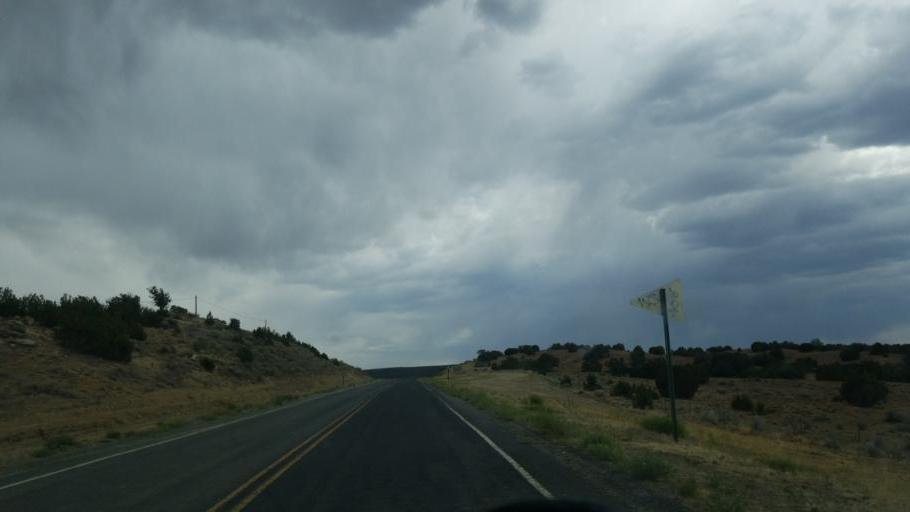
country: US
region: Arizona
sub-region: Apache County
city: Saint Michaels
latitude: 35.4240
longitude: -108.9788
